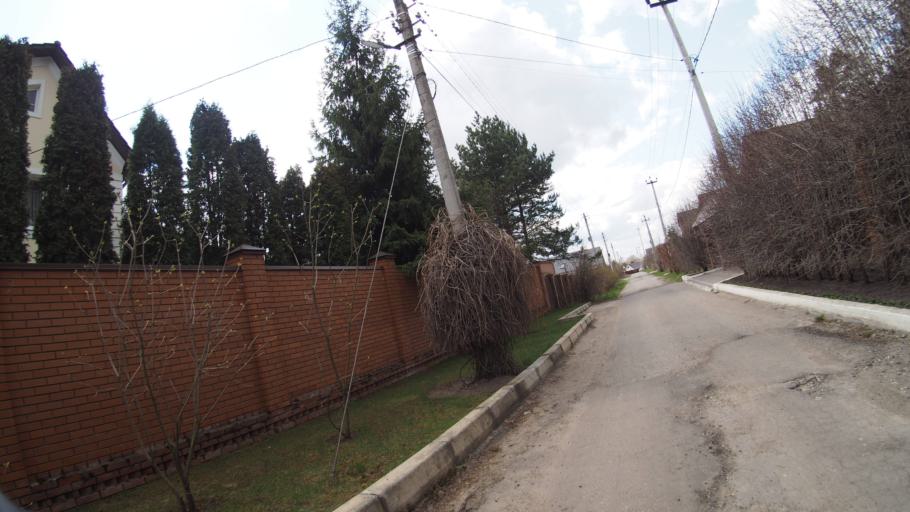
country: RU
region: Moskovskaya
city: Malyshevo
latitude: 55.5426
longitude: 38.3363
